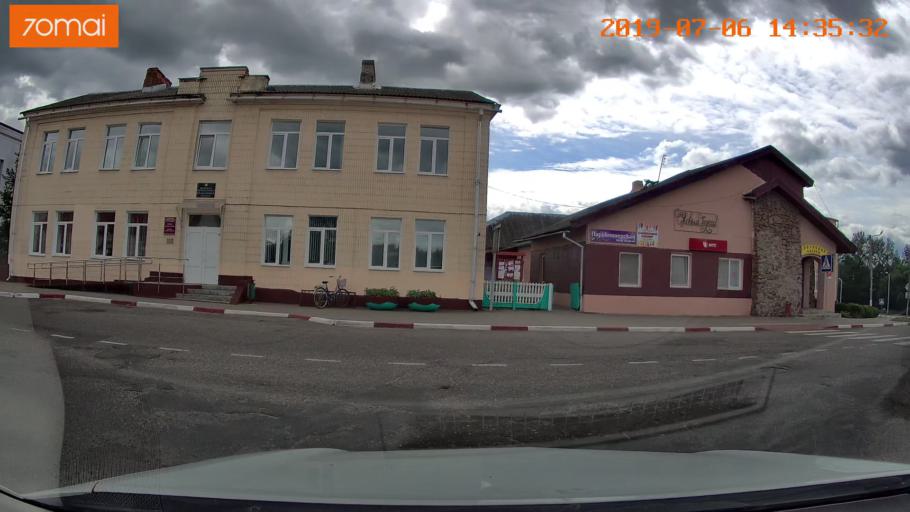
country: BY
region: Minsk
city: Ivyanyets
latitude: 53.8908
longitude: 26.7392
